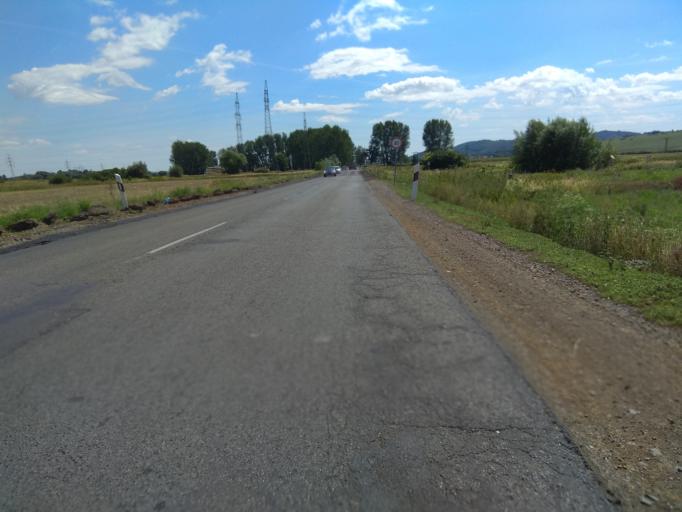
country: HU
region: Borsod-Abauj-Zemplen
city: Sajokaza
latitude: 48.2689
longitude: 20.5924
